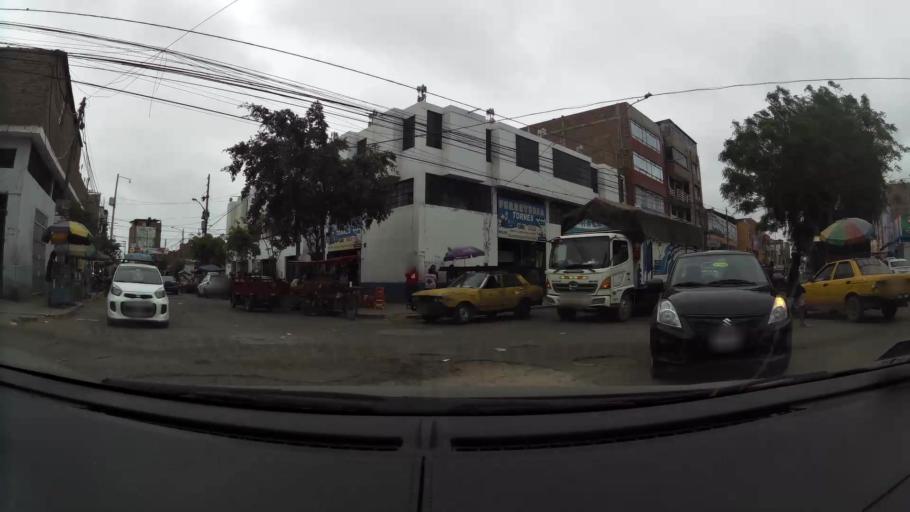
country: PE
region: La Libertad
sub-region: Provincia de Trujillo
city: Trujillo
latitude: -8.1132
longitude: -79.0174
